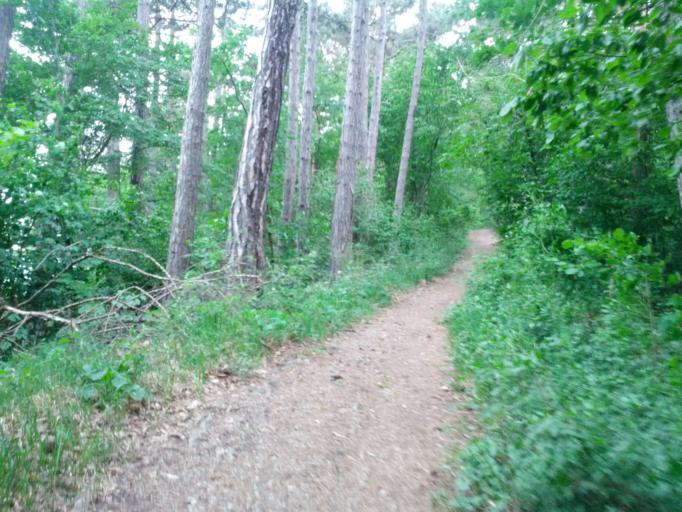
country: DE
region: Thuringia
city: Eisenach
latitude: 50.9875
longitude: 10.2939
